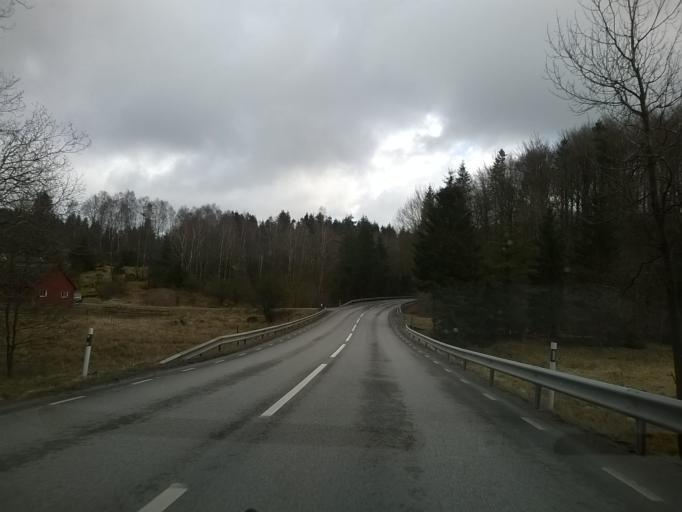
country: SE
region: Halland
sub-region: Varbergs Kommun
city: Tvaaker
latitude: 57.1494
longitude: 12.5683
